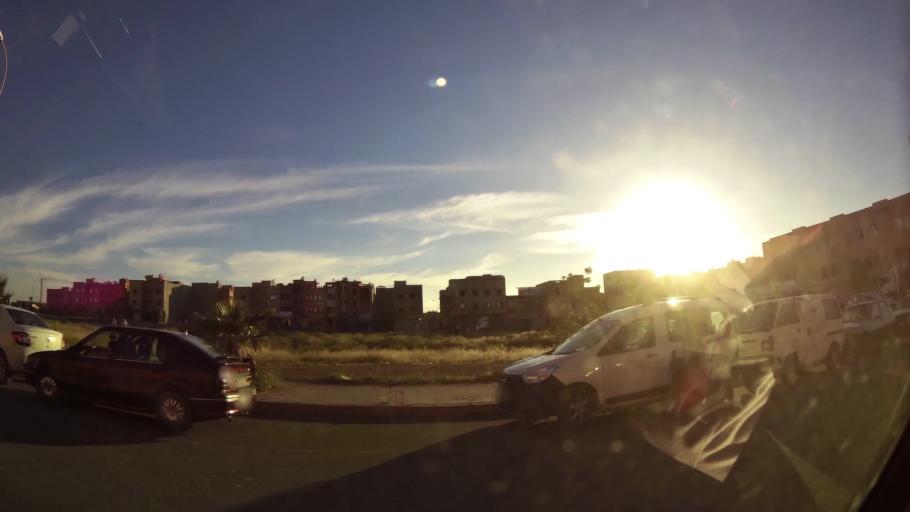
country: MA
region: Marrakech-Tensift-Al Haouz
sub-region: Marrakech
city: Marrakesh
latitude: 31.7493
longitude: -8.1137
